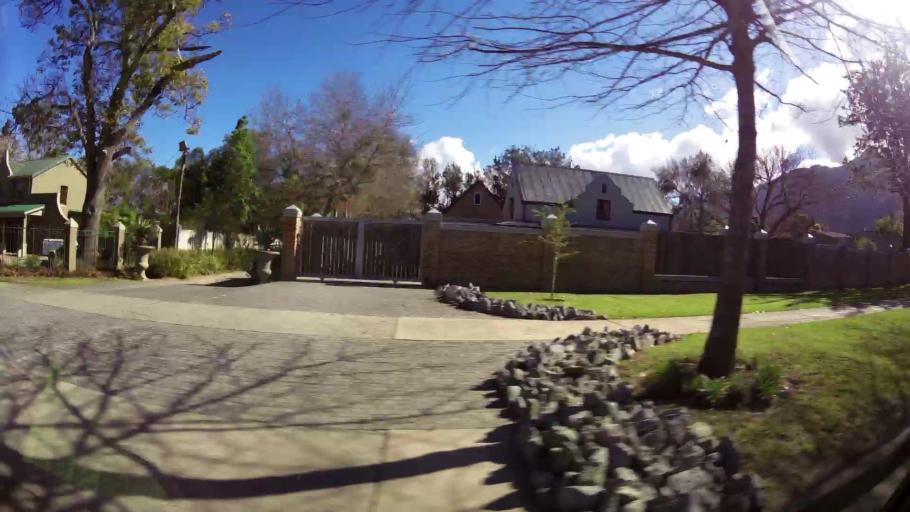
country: ZA
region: Western Cape
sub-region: Eden District Municipality
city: George
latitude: -33.9514
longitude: 22.4612
